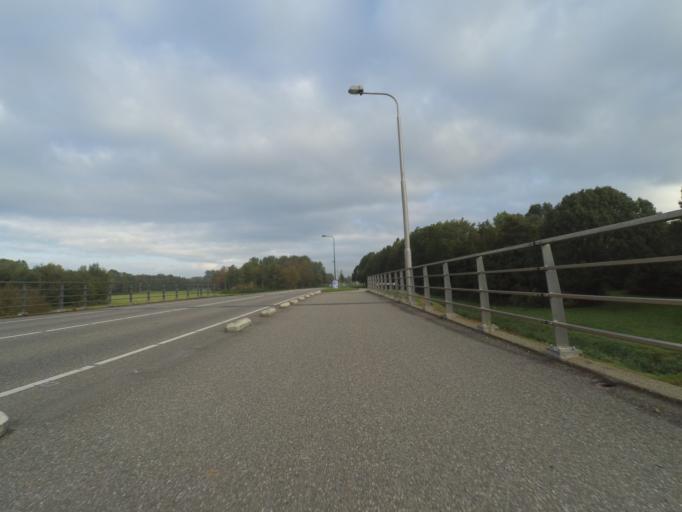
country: NL
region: Flevoland
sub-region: Gemeente Dronten
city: Dronten
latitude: 52.5247
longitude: 5.6961
